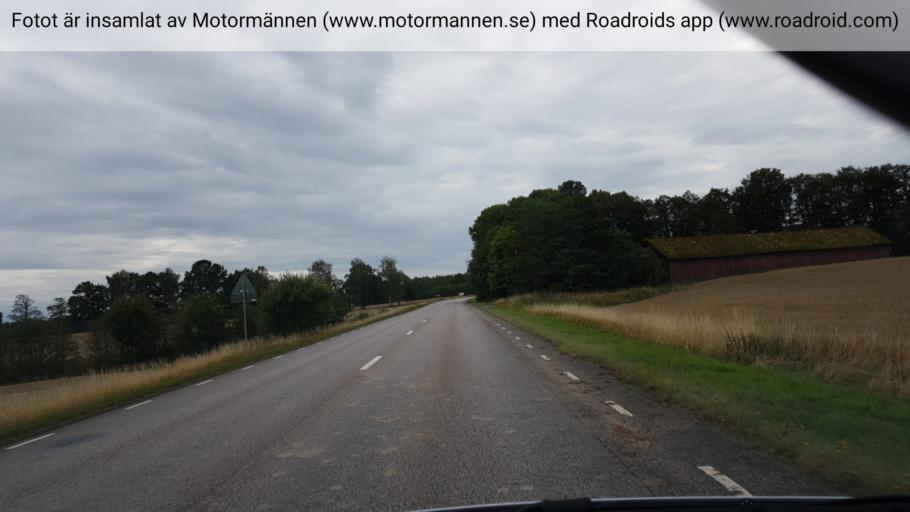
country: SE
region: Vaestra Goetaland
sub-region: Hjo Kommun
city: Hjo
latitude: 58.3260
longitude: 14.3212
